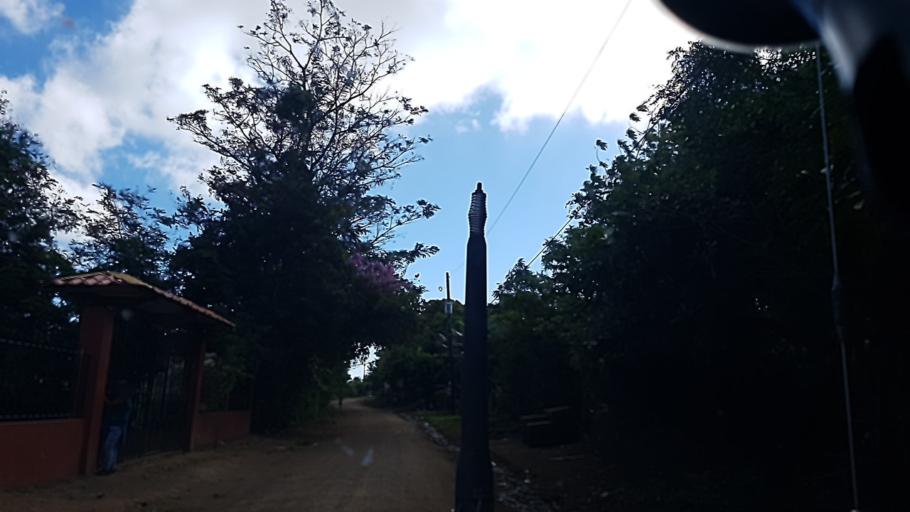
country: NI
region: Carazo
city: La Paz de Oriente
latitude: 11.8242
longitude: -86.1334
